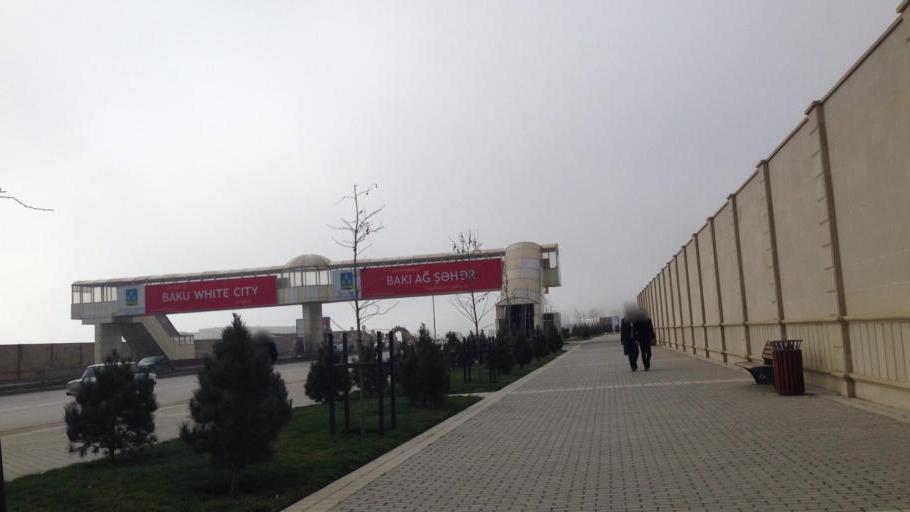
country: AZ
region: Baki
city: Baku
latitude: 40.3783
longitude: 49.8928
